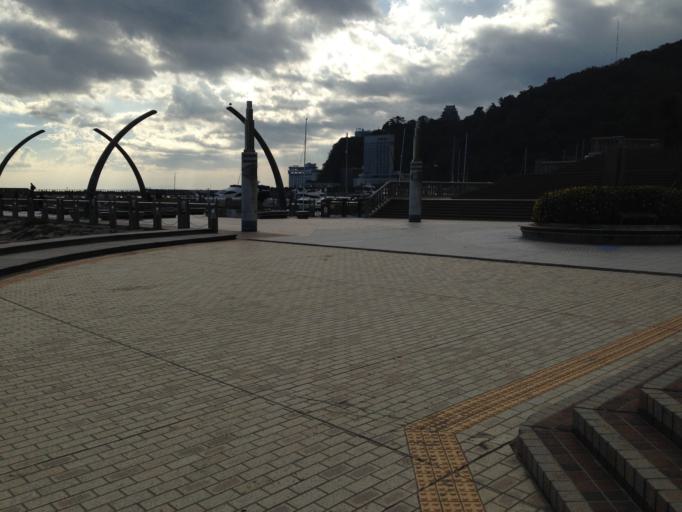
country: JP
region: Shizuoka
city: Atami
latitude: 35.0965
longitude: 139.0763
